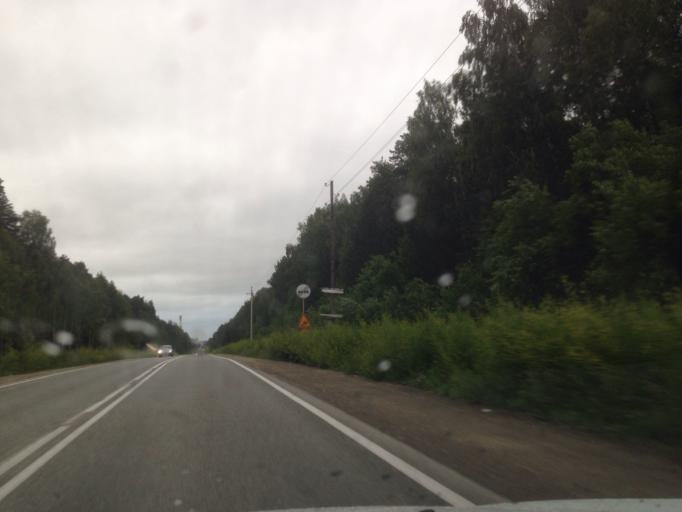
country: RU
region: Sverdlovsk
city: Istok
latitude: 56.8393
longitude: 60.7750
